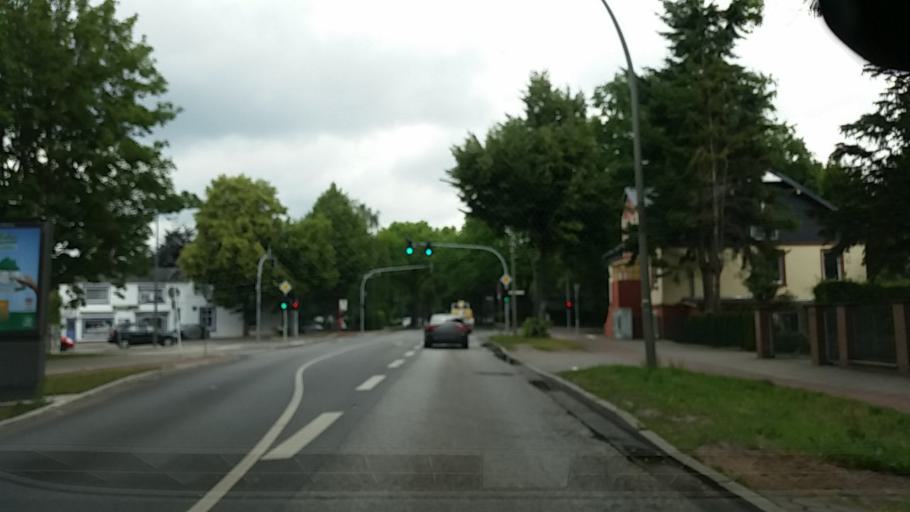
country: DE
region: Hamburg
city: Eidelstedt
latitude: 53.6268
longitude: 9.9097
